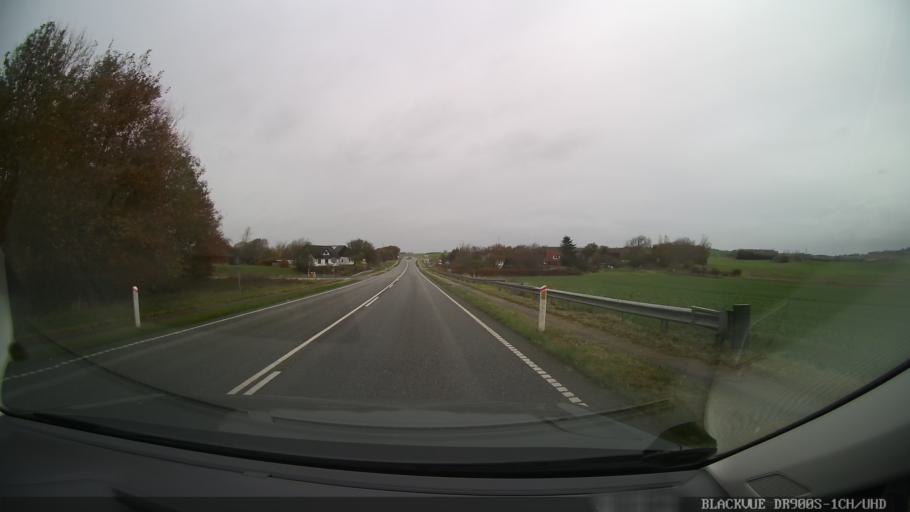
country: DK
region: North Denmark
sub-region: Thisted Kommune
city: Thisted
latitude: 56.8523
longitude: 8.6996
